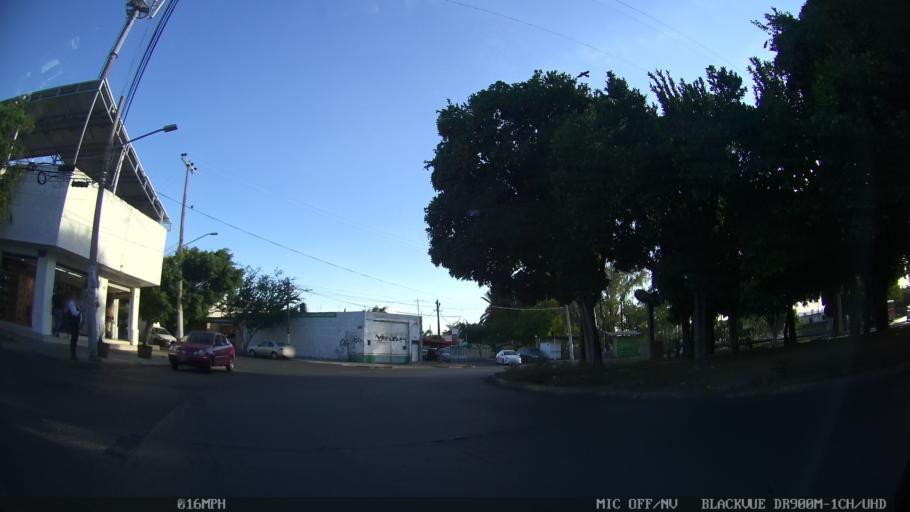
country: MX
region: Jalisco
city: Tlaquepaque
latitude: 20.6947
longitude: -103.3087
